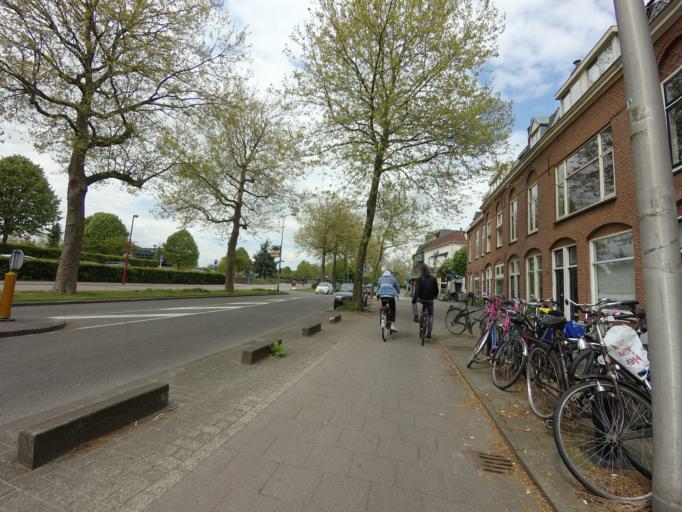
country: NL
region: Utrecht
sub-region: Gemeente Utrecht
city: Utrecht
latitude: 52.0992
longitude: 5.1292
